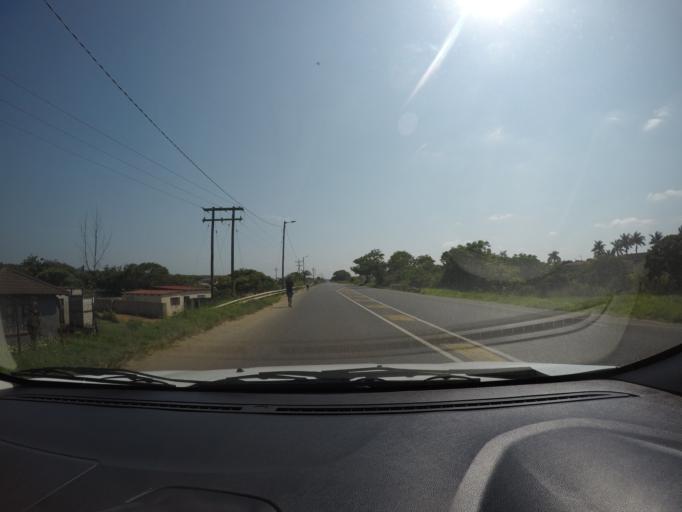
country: ZA
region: KwaZulu-Natal
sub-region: uThungulu District Municipality
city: eSikhawini
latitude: -28.8855
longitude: 31.8853
